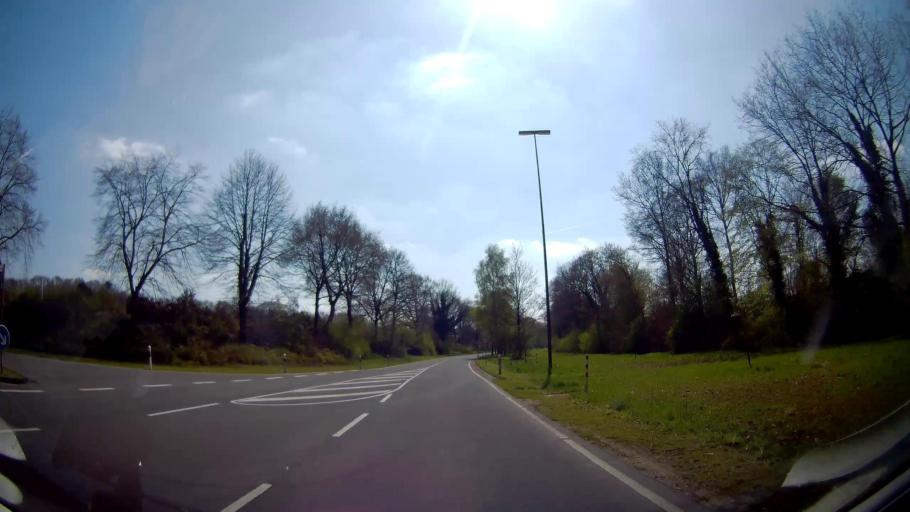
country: DE
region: North Rhine-Westphalia
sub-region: Regierungsbezirk Munster
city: Klein Reken
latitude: 51.7329
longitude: 7.0483
